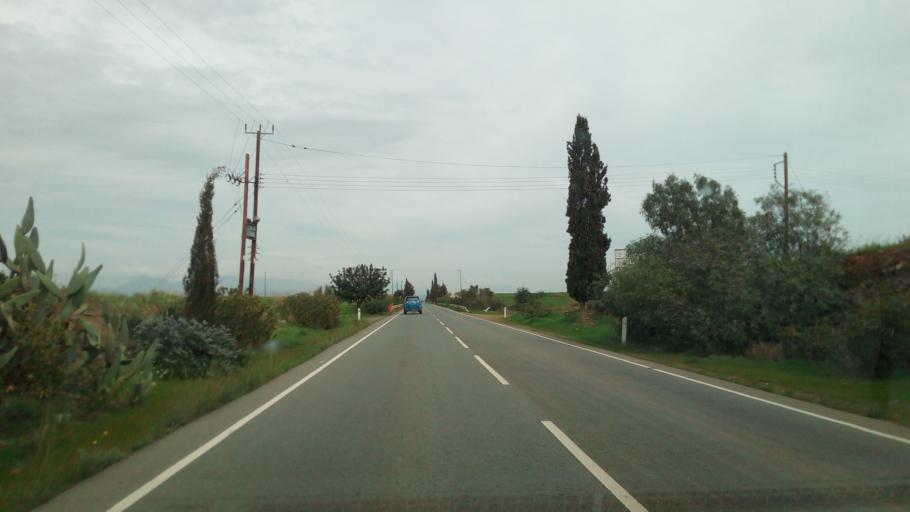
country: CY
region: Lefkosia
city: Astromeritis
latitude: 35.1082
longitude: 32.9834
